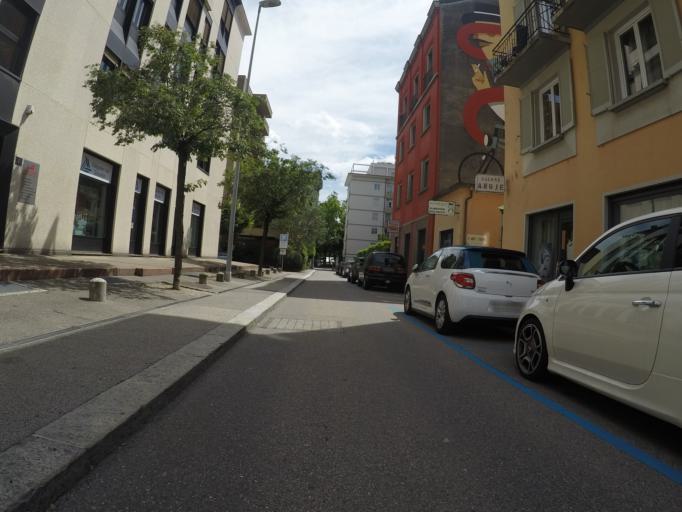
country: CH
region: Ticino
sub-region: Lugano District
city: Lugano
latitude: 46.0066
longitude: 8.9581
